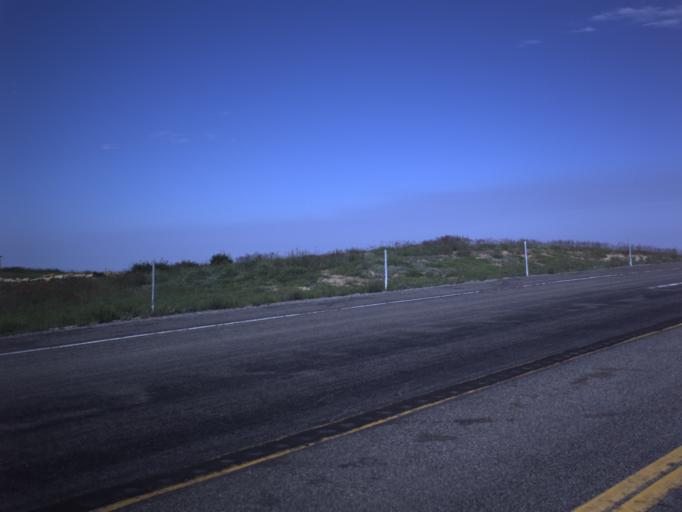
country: US
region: Utah
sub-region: Sanpete County
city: Fairview
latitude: 39.6170
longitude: -111.3101
